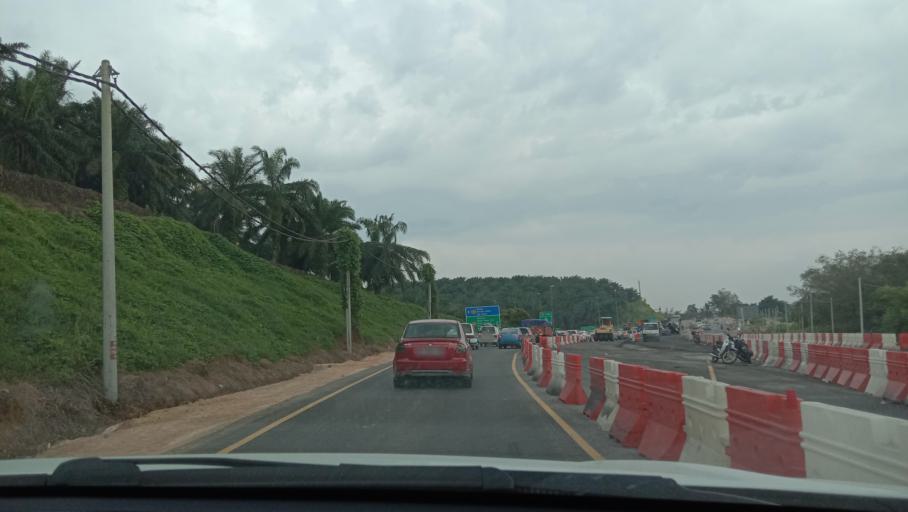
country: MY
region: Selangor
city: Batu Arang
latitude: 3.2616
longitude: 101.4629
